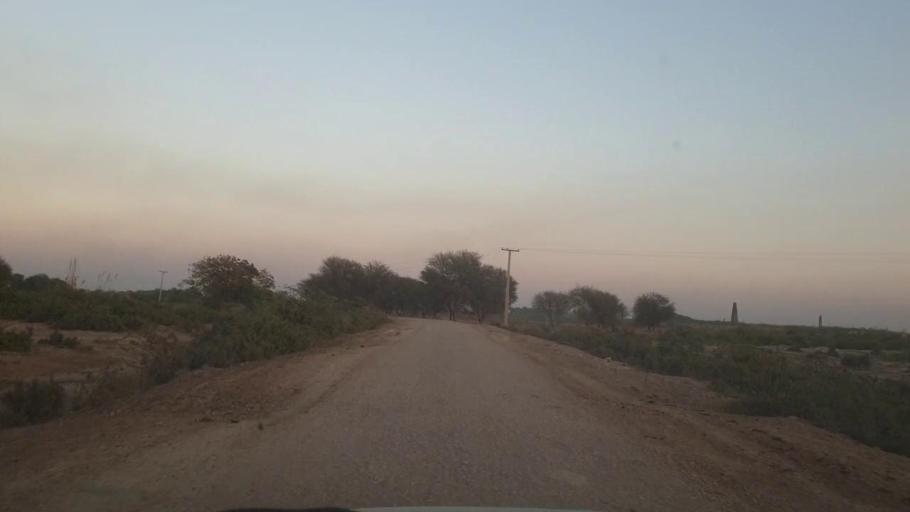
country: PK
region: Sindh
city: Mirpur Khas
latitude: 25.4974
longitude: 69.0392
